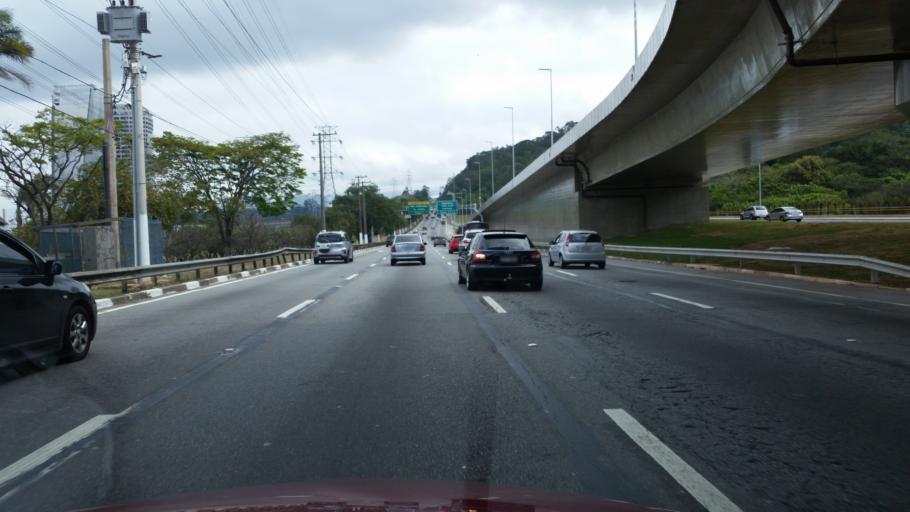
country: BR
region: Sao Paulo
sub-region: Taboao Da Serra
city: Taboao da Serra
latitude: -23.6333
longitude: -46.7196
